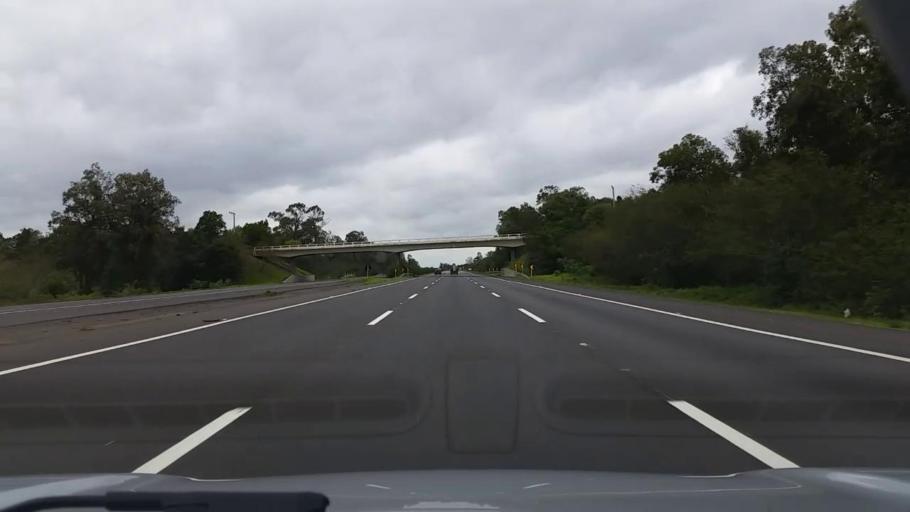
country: BR
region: Rio Grande do Sul
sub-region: Rolante
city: Rolante
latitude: -29.8849
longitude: -50.5761
